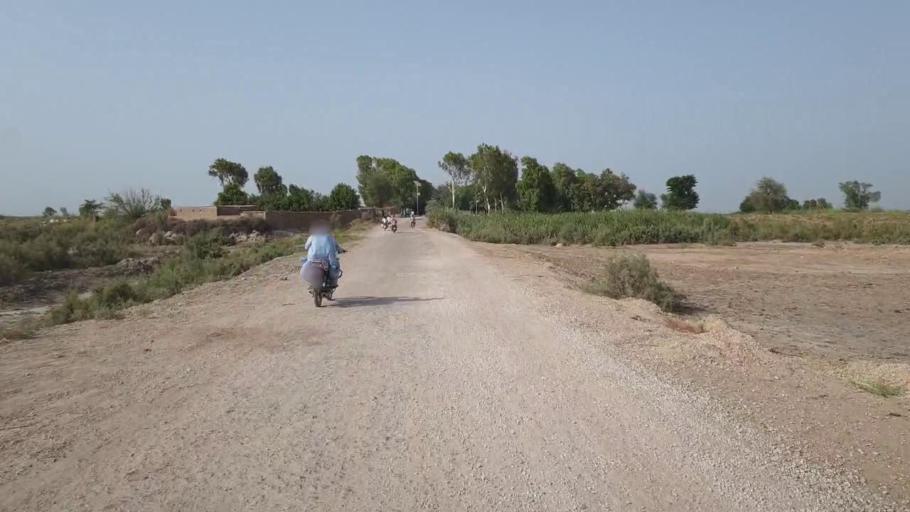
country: PK
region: Sindh
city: Daur
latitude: 26.3486
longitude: 68.1720
